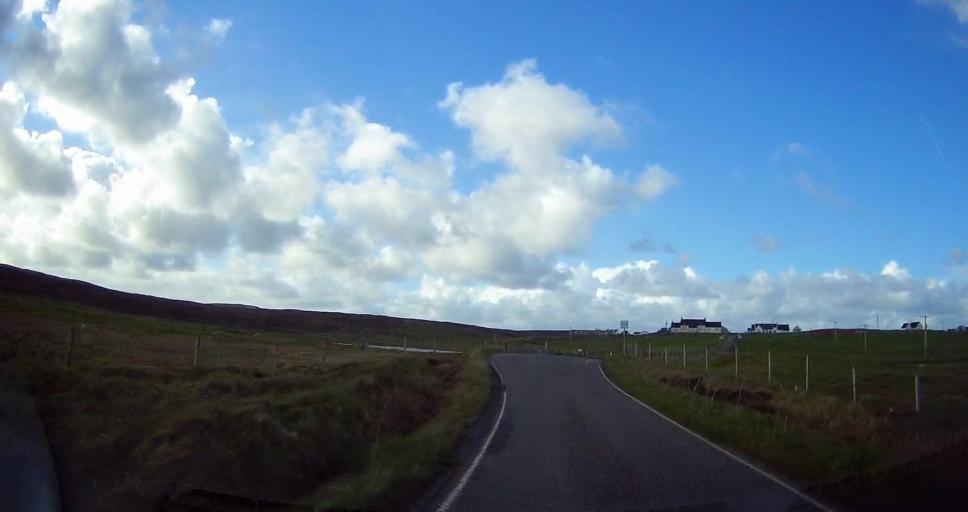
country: GB
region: Scotland
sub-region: Shetland Islands
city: Shetland
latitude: 60.3653
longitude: -1.1419
